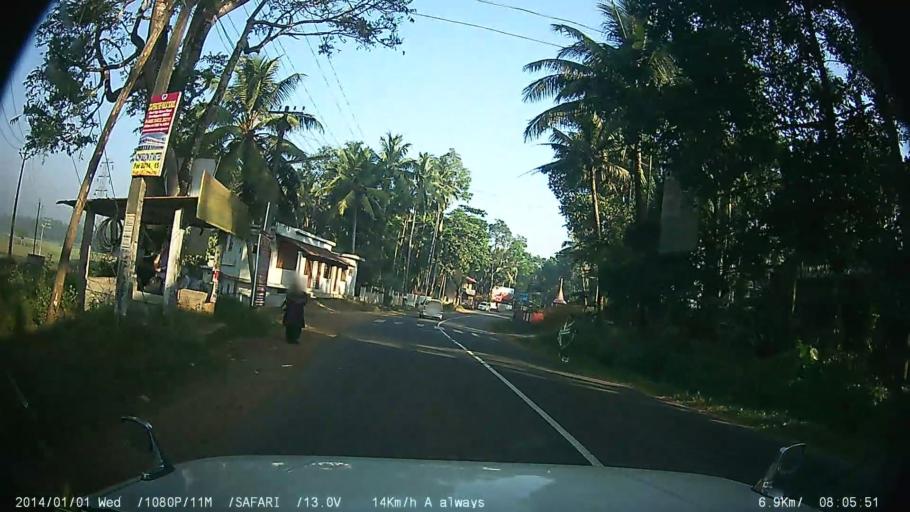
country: IN
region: Kerala
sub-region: Ernakulam
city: Muvattupuzha
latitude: 9.9495
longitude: 76.5763
